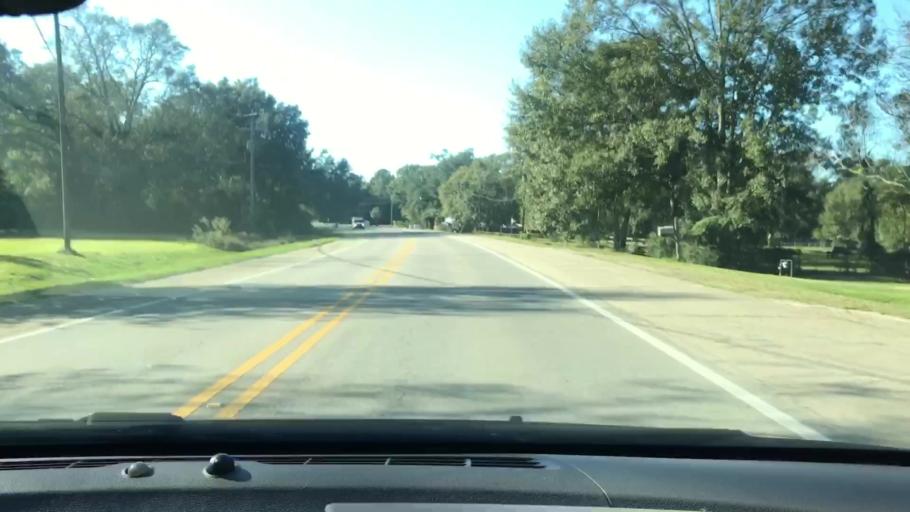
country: US
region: Louisiana
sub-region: Saint Tammany Parish
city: Pearl River
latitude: 30.4281
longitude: -89.7871
